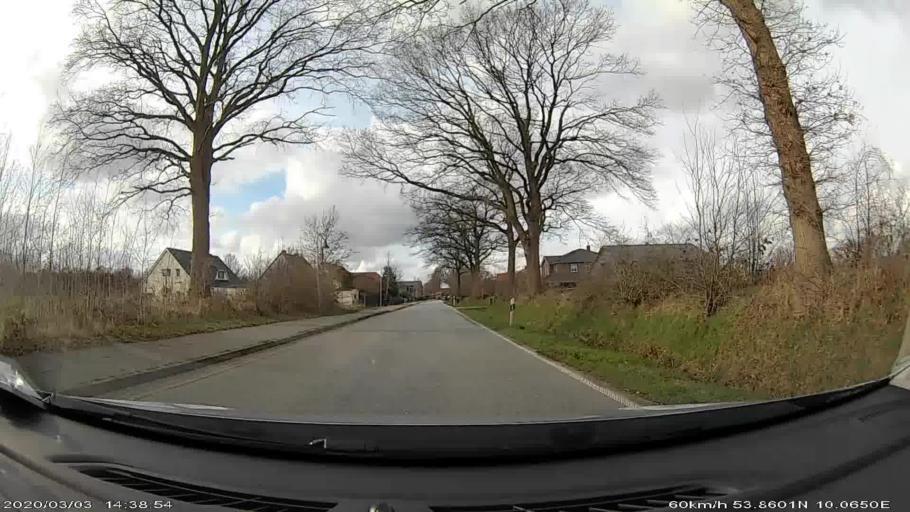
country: DE
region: Schleswig-Holstein
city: Struvenhutten
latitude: 53.8602
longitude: 10.0649
